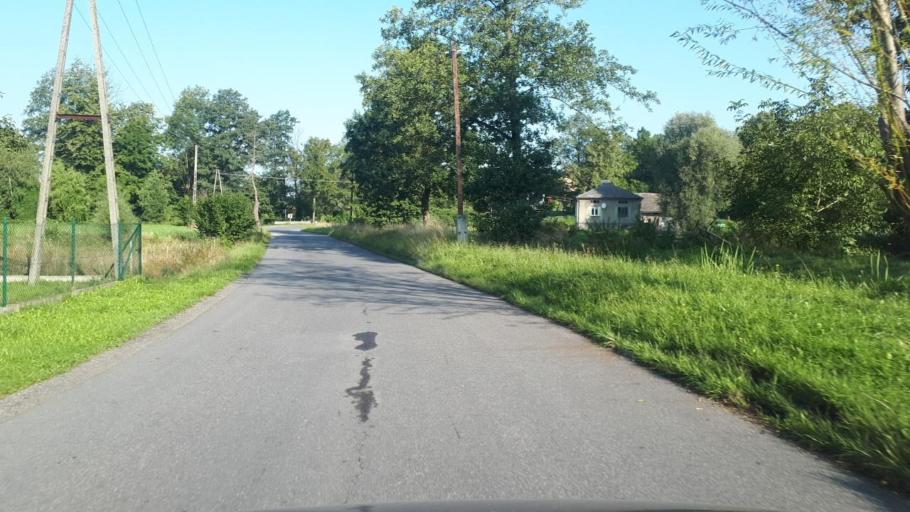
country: PL
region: Silesian Voivodeship
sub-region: Powiat cieszynski
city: Chybie
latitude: 49.8674
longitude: 18.8585
